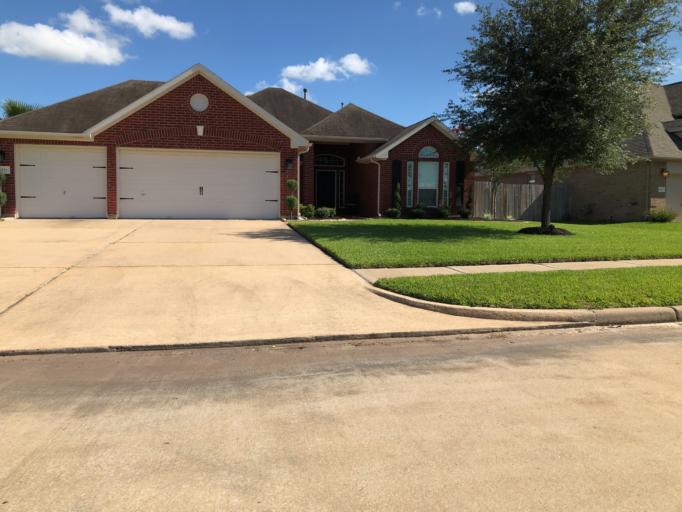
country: US
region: Texas
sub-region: Harris County
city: Katy
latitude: 29.8065
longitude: -95.8320
